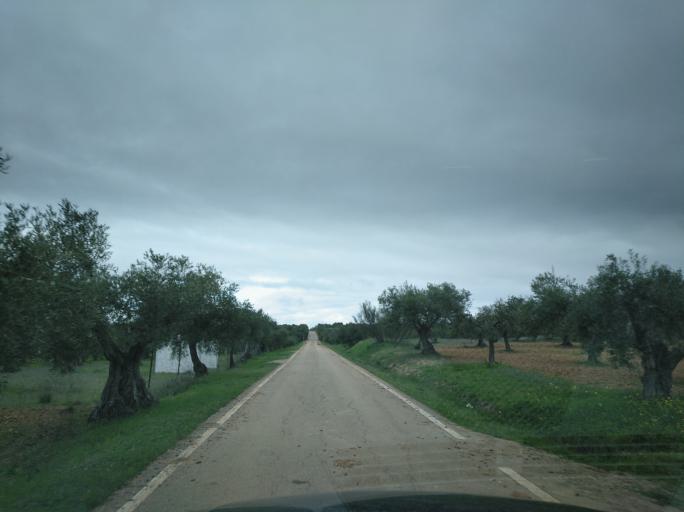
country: PT
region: Portalegre
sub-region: Campo Maior
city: Campo Maior
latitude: 38.9844
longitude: -7.0375
